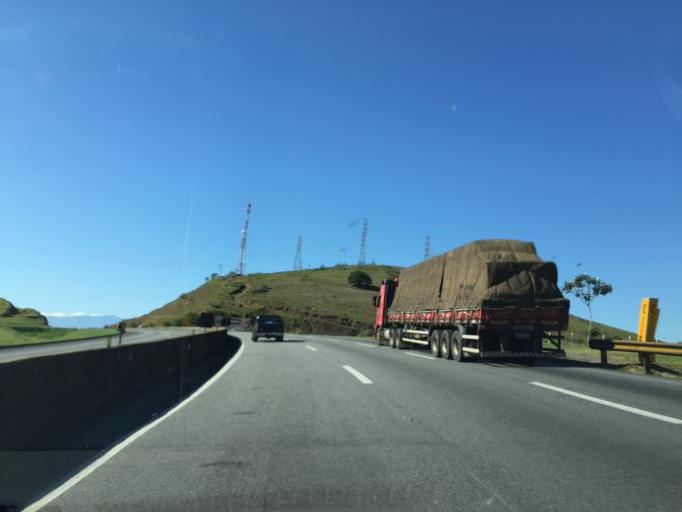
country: BR
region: Sao Paulo
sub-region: Cruzeiro
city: Cruzeiro
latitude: -22.6397
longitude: -44.9387
